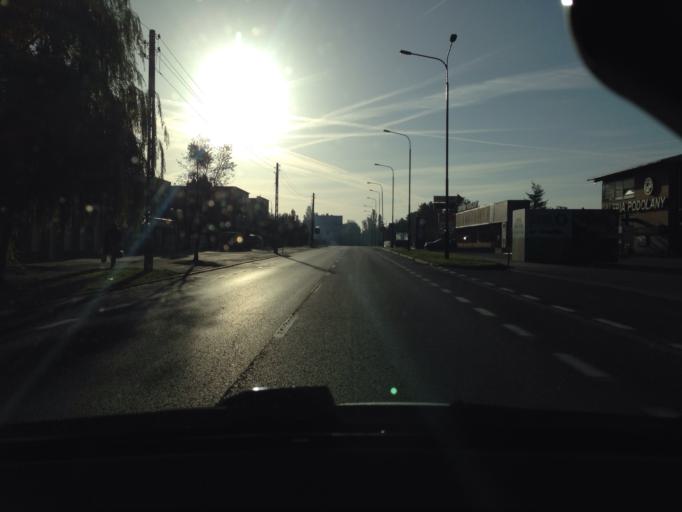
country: PL
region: Greater Poland Voivodeship
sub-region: Powiat poznanski
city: Suchy Las
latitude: 52.4495
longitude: 16.8935
